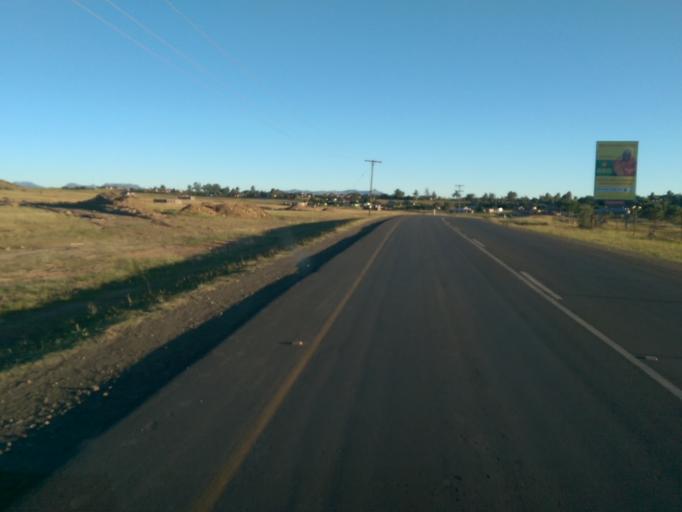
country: LS
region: Maseru
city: Maseru
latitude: -29.3839
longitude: 27.5608
